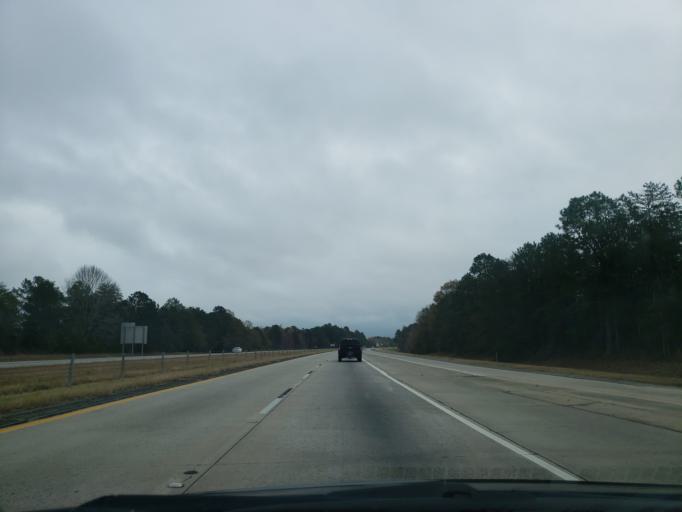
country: US
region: Georgia
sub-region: Treutlen County
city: Soperton
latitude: 32.4342
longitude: -82.6034
